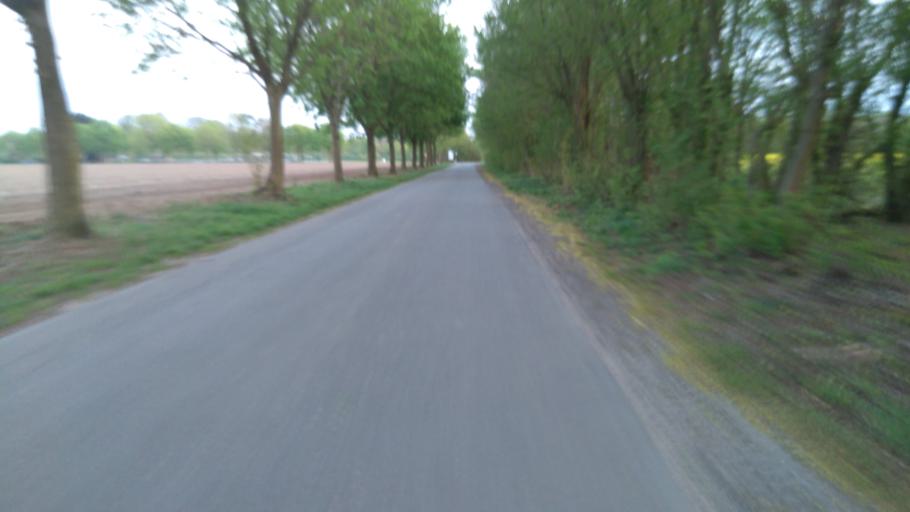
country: DE
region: Lower Saxony
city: Bargstedt
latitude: 53.4671
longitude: 9.4674
